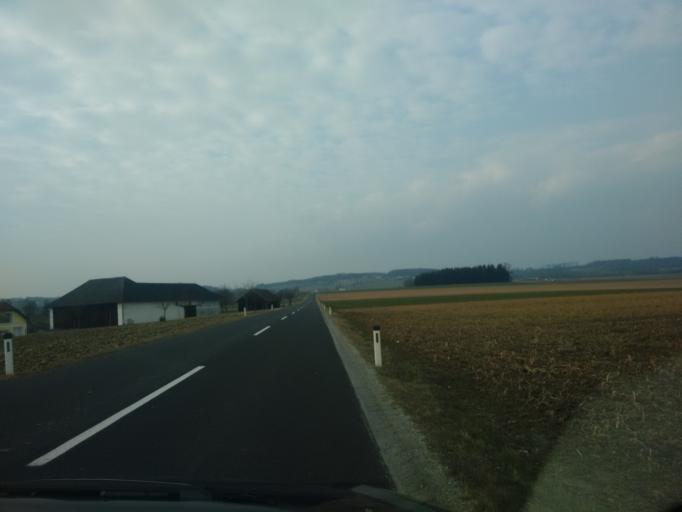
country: AT
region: Upper Austria
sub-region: Wels-Land
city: Holzhausen
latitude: 48.2242
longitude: 14.0732
